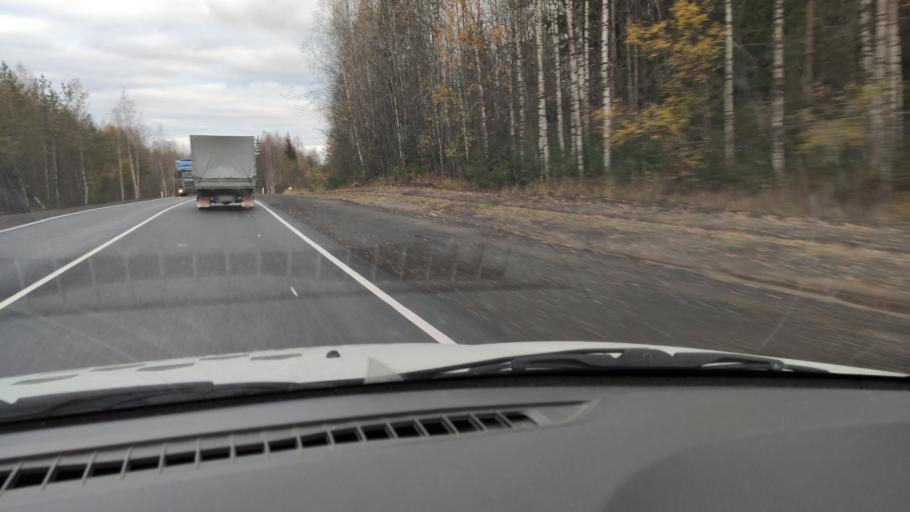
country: RU
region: Kirov
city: Chernaya Kholunitsa
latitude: 58.8734
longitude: 51.5100
